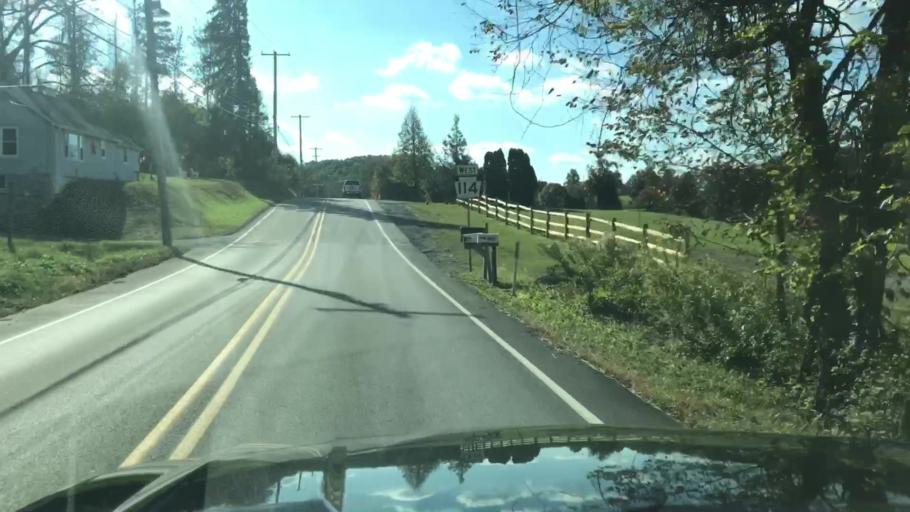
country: US
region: Pennsylvania
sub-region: Cumberland County
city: Lower Allen
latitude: 40.1932
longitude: -76.8903
